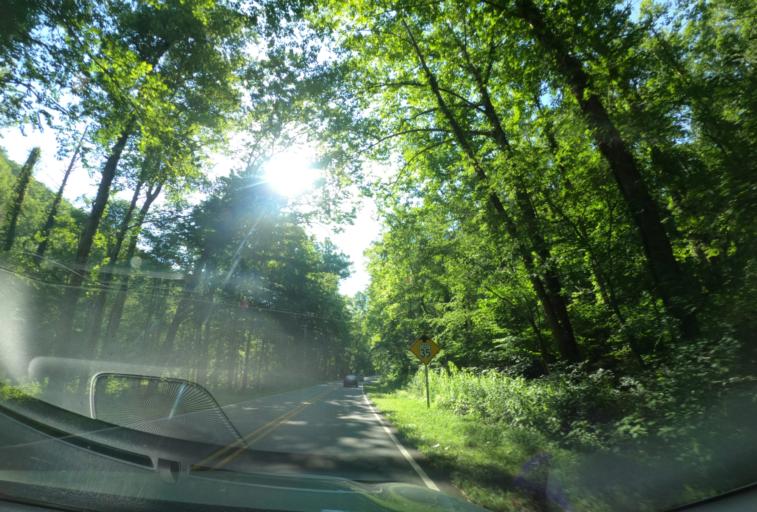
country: US
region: North Carolina
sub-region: Transylvania County
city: Brevard
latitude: 35.2899
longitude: -82.7665
